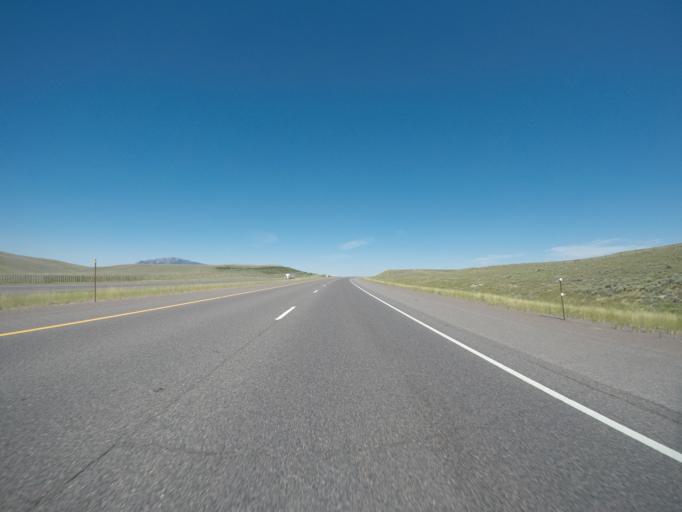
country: US
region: Wyoming
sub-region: Carbon County
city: Saratoga
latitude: 41.6449
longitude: -106.3200
